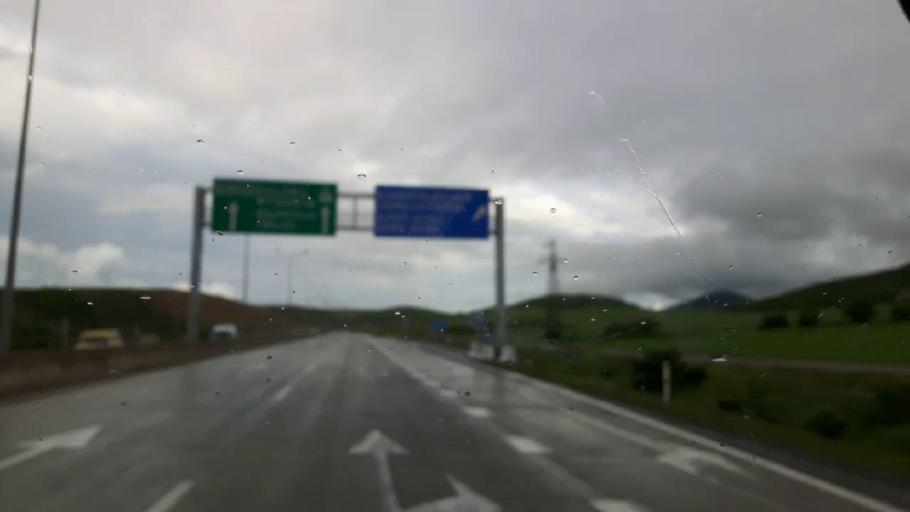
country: GE
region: Shida Kartli
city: Kaspi
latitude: 41.9999
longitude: 44.3889
